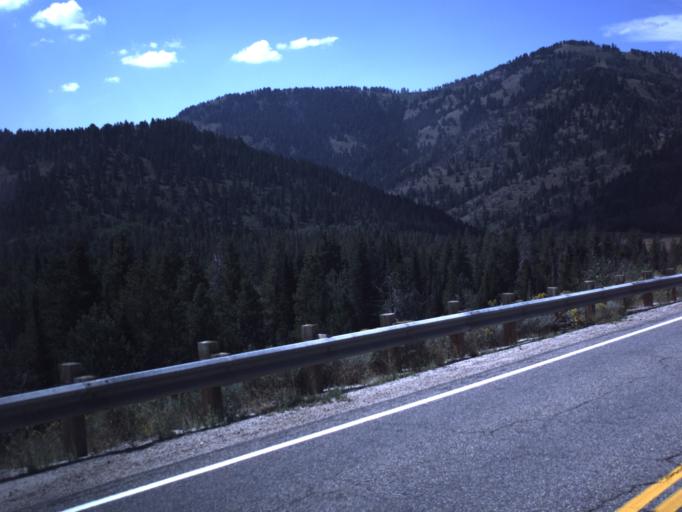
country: US
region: Idaho
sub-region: Bear Lake County
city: Paris
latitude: 41.9597
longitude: -111.5180
